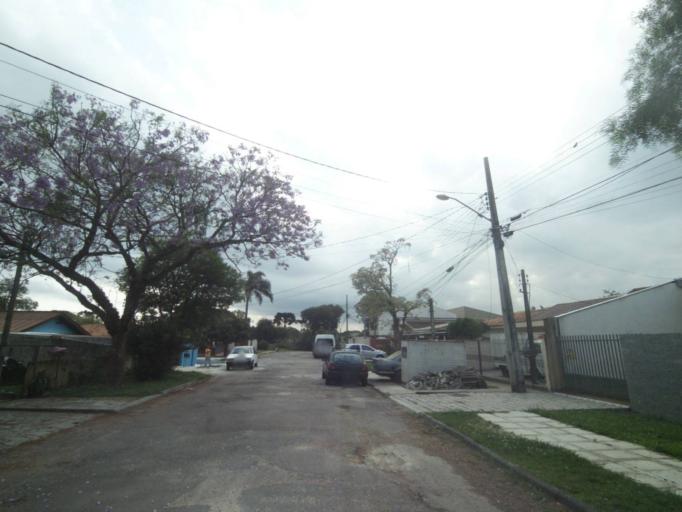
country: BR
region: Parana
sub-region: Pinhais
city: Pinhais
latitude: -25.4170
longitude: -49.2163
